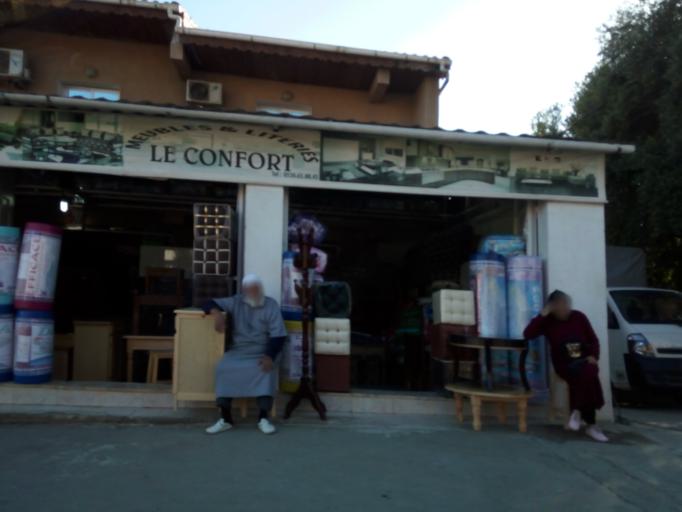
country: DZ
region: Tipaza
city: Saoula
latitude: 36.7190
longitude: 3.0111
